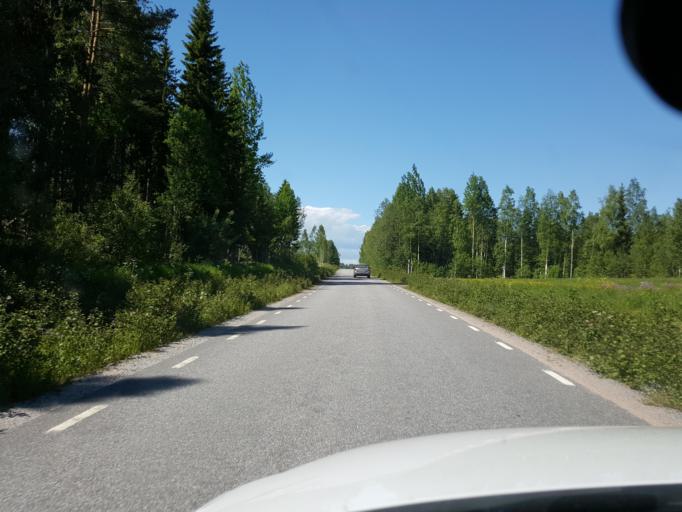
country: SE
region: Gaevleborg
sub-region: Ljusdals Kommun
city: Jaervsoe
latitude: 61.7304
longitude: 16.2847
